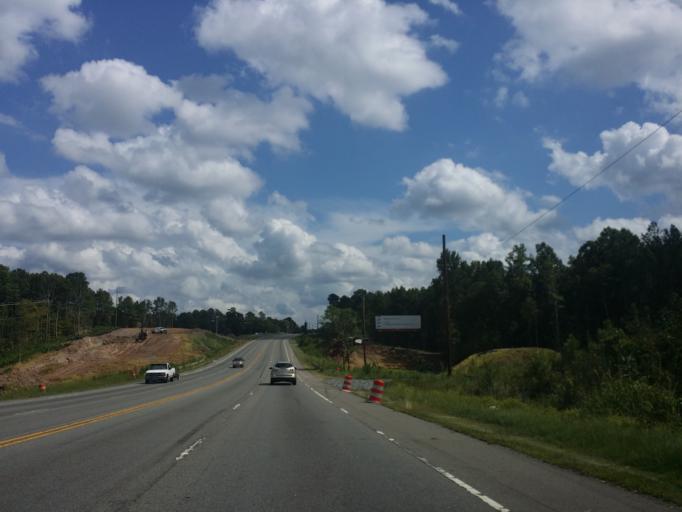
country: US
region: North Carolina
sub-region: Durham County
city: Durham
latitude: 35.9738
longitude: -78.8524
